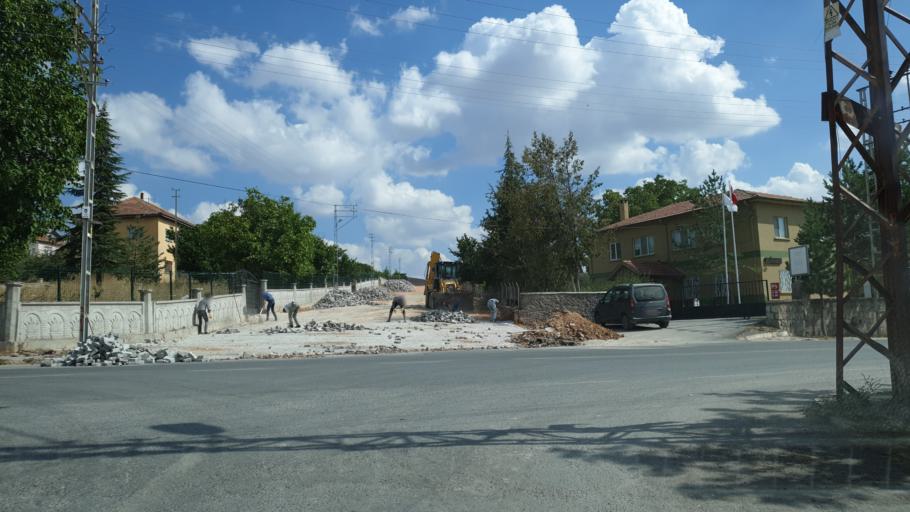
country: TR
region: Kayseri
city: Felahiye
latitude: 39.0886
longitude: 35.5644
